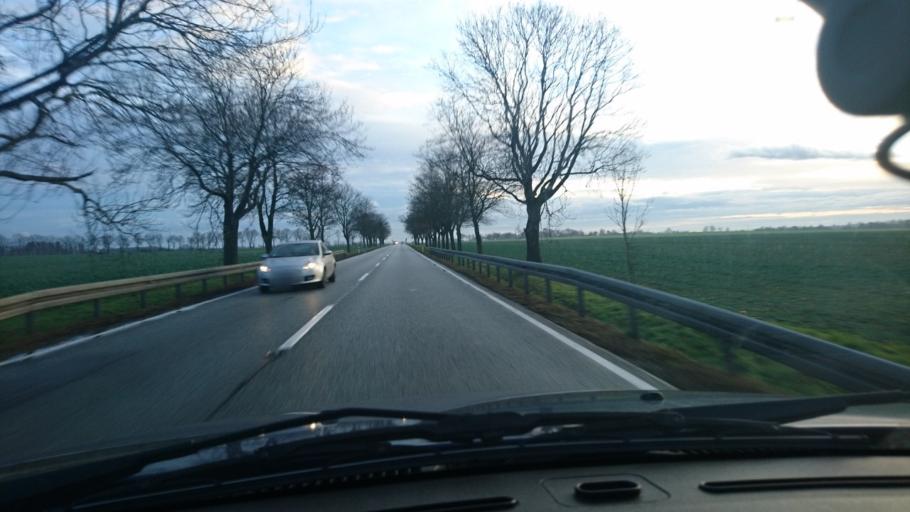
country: PL
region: Opole Voivodeship
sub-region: Powiat kluczborski
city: Byczyna
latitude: 51.0748
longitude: 18.2016
